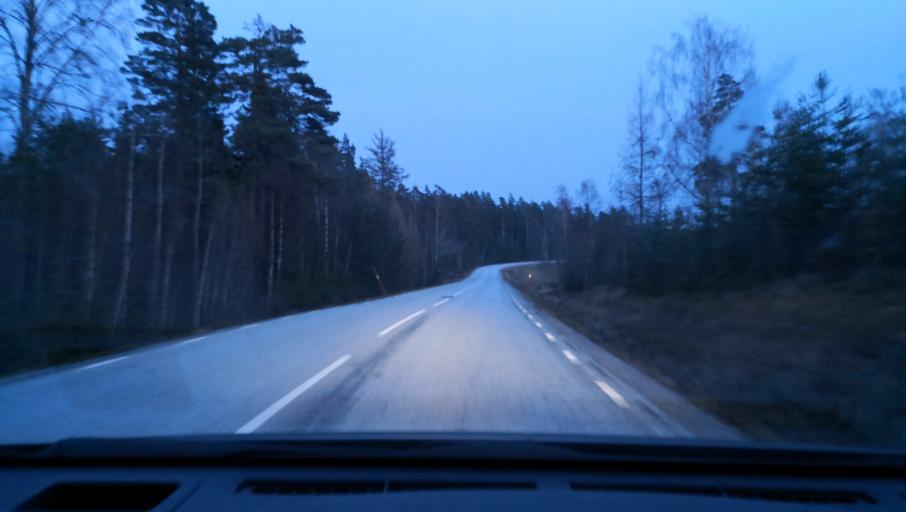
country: SE
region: OErebro
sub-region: Lindesbergs Kommun
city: Frovi
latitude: 59.5893
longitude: 15.4346
